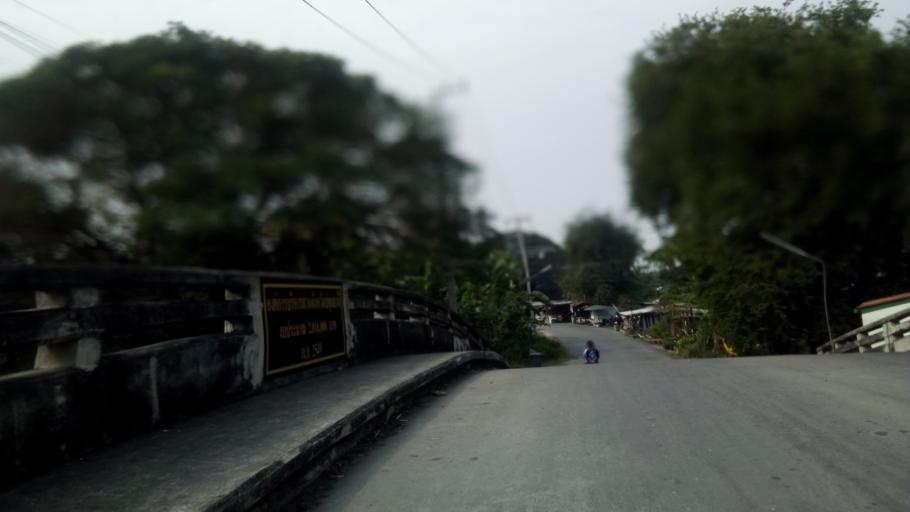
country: TH
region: Pathum Thani
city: Nong Suea
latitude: 14.0599
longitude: 100.8468
